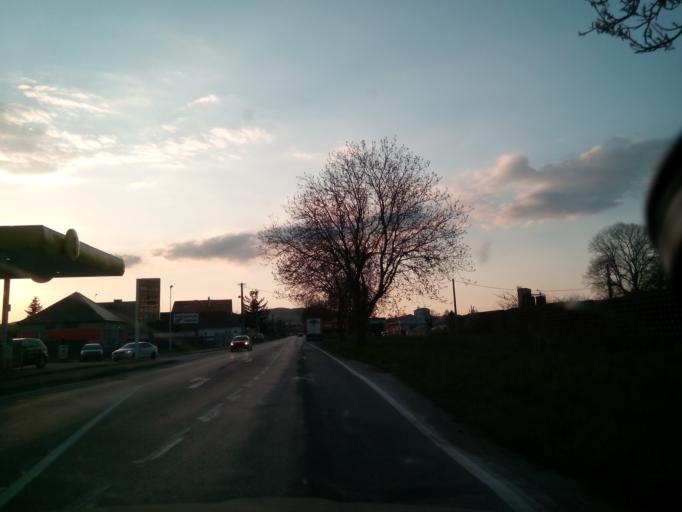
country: SK
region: Trnavsky
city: Vrbove
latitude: 48.6137
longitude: 17.7366
